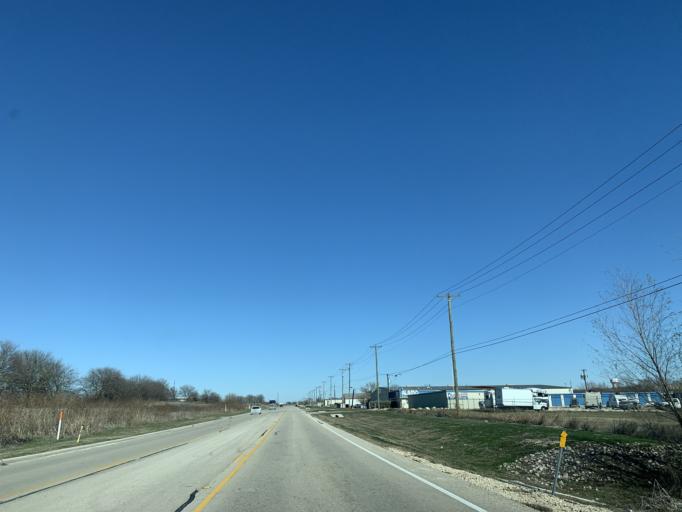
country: US
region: Texas
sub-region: Williamson County
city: Hutto
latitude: 30.5441
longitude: -97.5734
